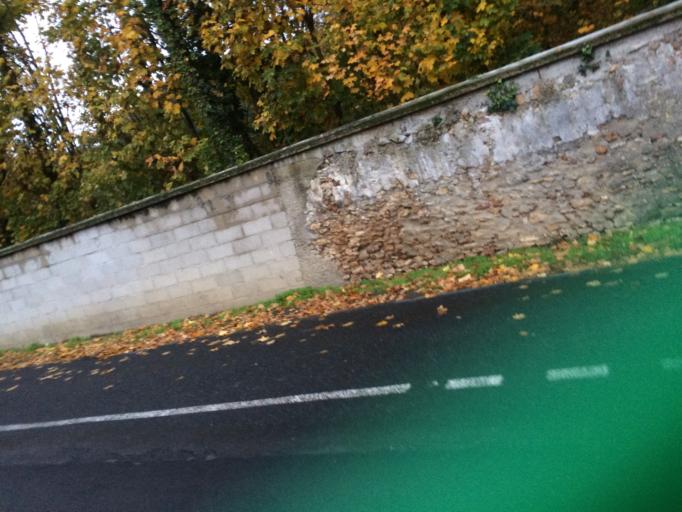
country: FR
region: Ile-de-France
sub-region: Departement de l'Essonne
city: La Ville-du-Bois
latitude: 48.6593
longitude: 2.2638
